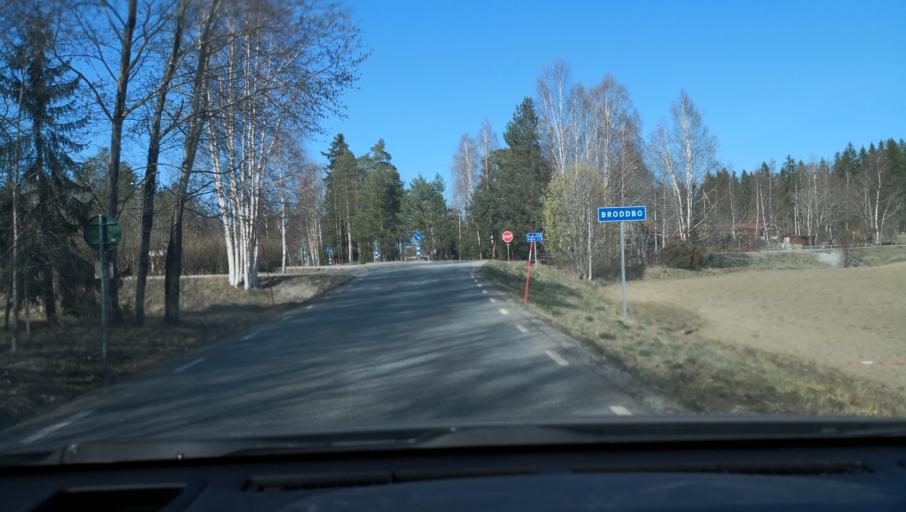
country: SE
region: Vaestmanland
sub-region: Sala Kommun
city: Sala
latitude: 59.9838
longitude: 16.4758
